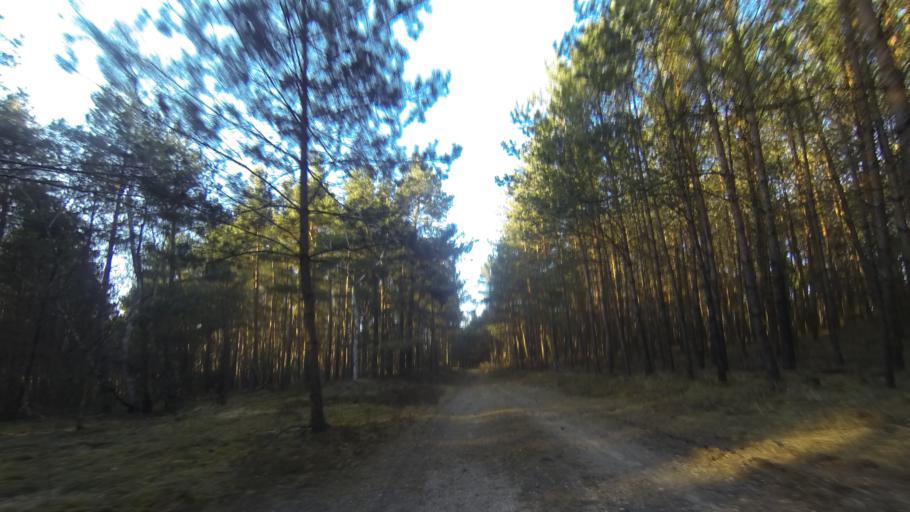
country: DE
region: Saxony
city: Ottendorf-Okrilla
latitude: 51.2038
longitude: 13.8027
